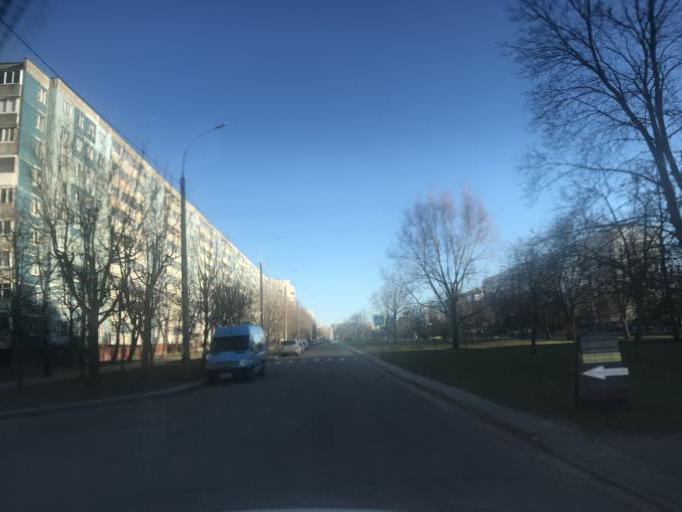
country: BY
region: Mogilev
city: Mahilyow
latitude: 53.8734
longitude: 30.3339
